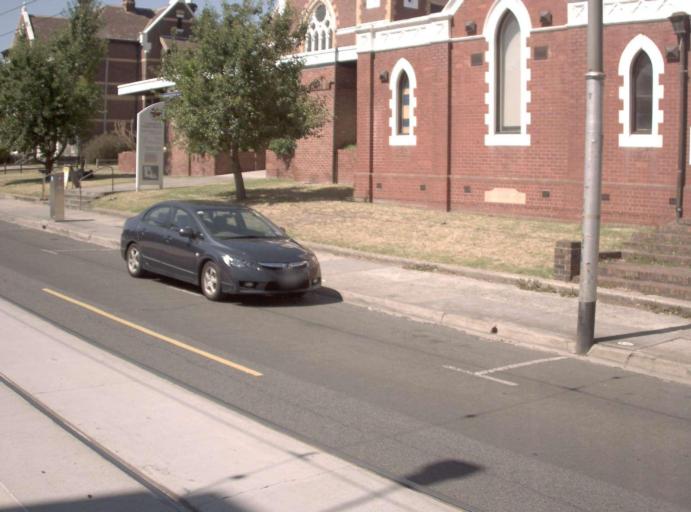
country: AU
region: Victoria
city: Glenferrie
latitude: -37.8329
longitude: 145.0586
